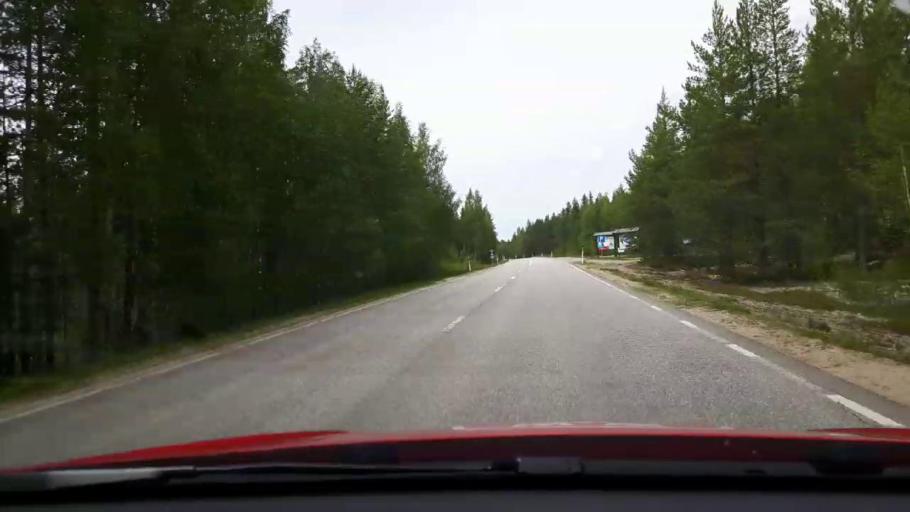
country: SE
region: Jaemtland
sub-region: Harjedalens Kommun
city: Sveg
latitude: 62.1190
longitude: 14.1701
